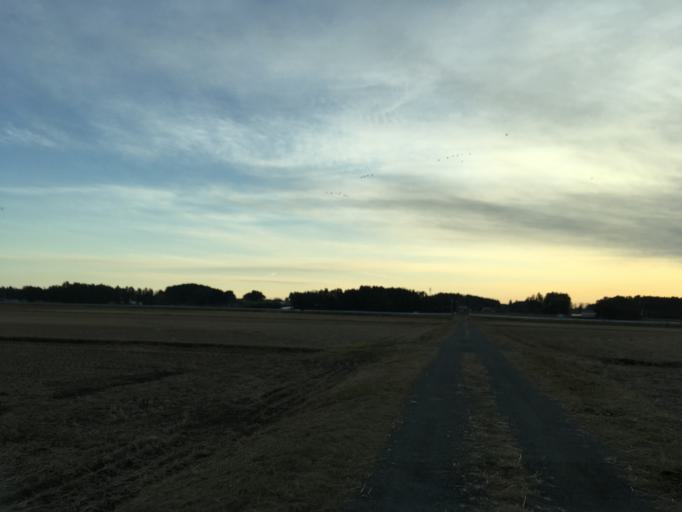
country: JP
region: Miyagi
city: Kogota
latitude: 38.6456
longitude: 141.0632
